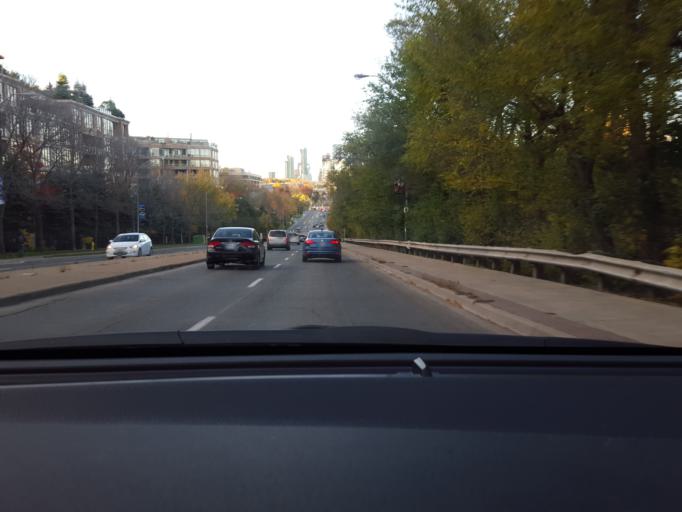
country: CA
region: Ontario
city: Willowdale
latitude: 43.7373
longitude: -79.4051
